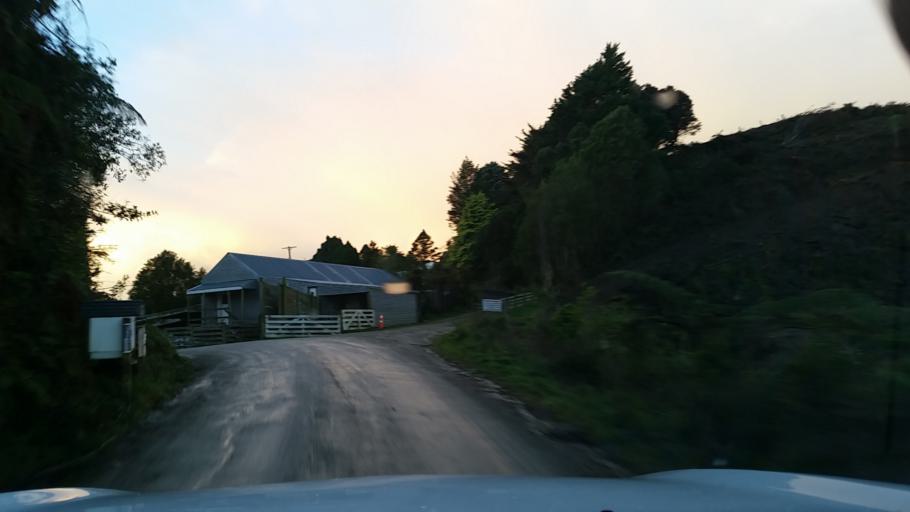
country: NZ
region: Manawatu-Wanganui
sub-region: Wanganui District
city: Wanganui
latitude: -39.7708
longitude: 174.8718
